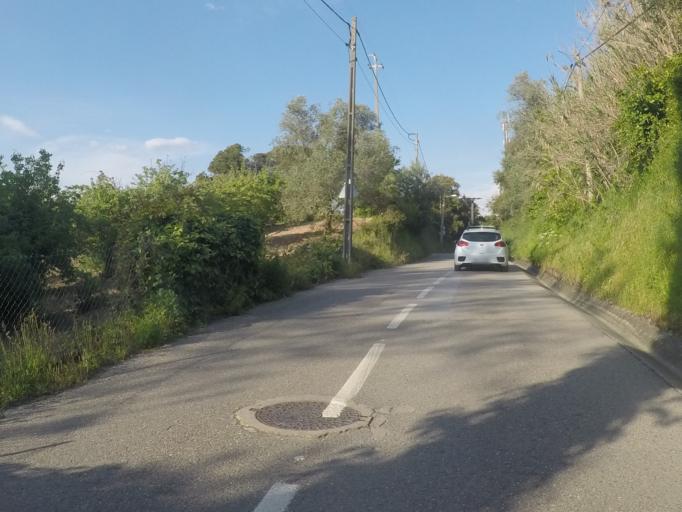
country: PT
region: Setubal
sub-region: Sesimbra
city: Sesimbra
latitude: 38.4689
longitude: -9.1718
